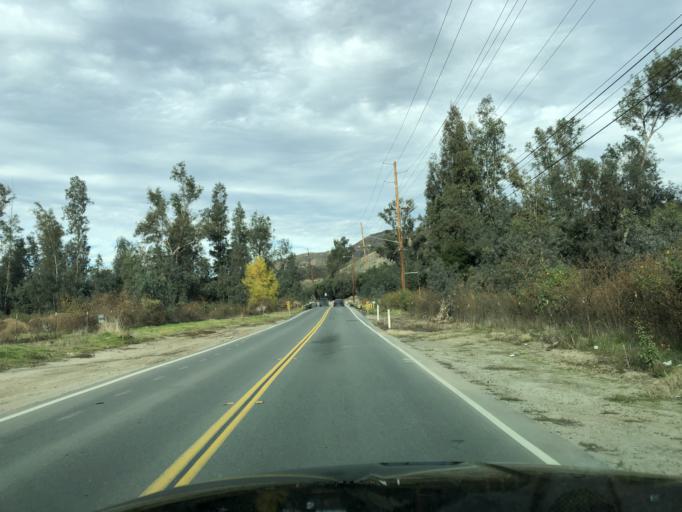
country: US
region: California
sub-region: Riverside County
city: Lake Elsinore
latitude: 33.7280
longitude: -117.3953
